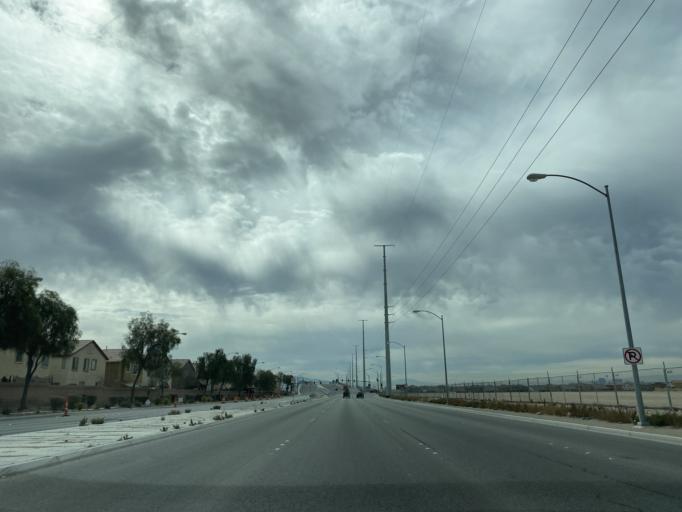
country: US
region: Nevada
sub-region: Clark County
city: Nellis Air Force Base
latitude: 36.2721
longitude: -115.0800
